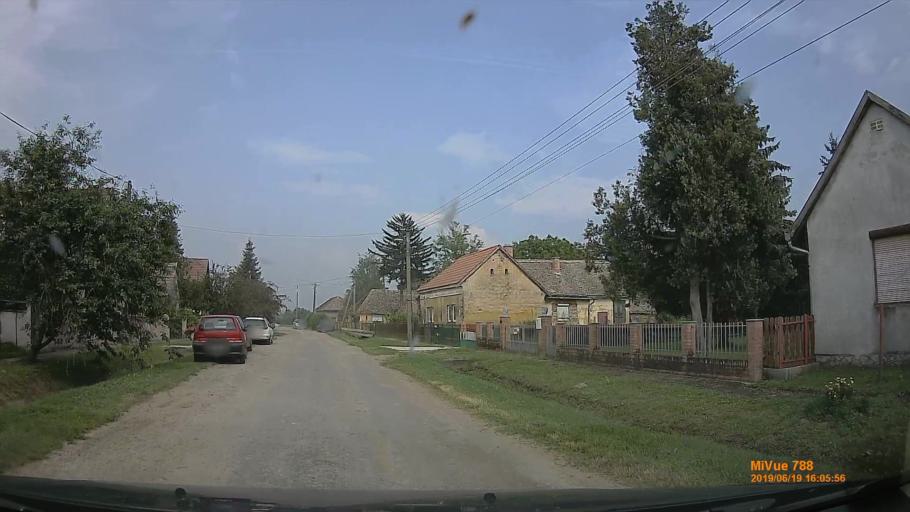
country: HU
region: Baranya
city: Szigetvar
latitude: 46.0737
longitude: 17.7858
